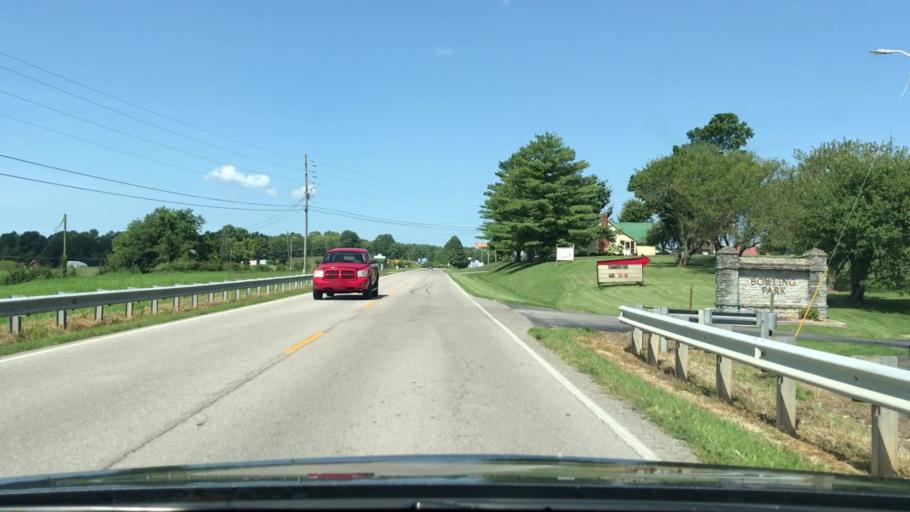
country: US
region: Kentucky
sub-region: Metcalfe County
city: Edmonton
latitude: 36.9886
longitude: -85.6482
